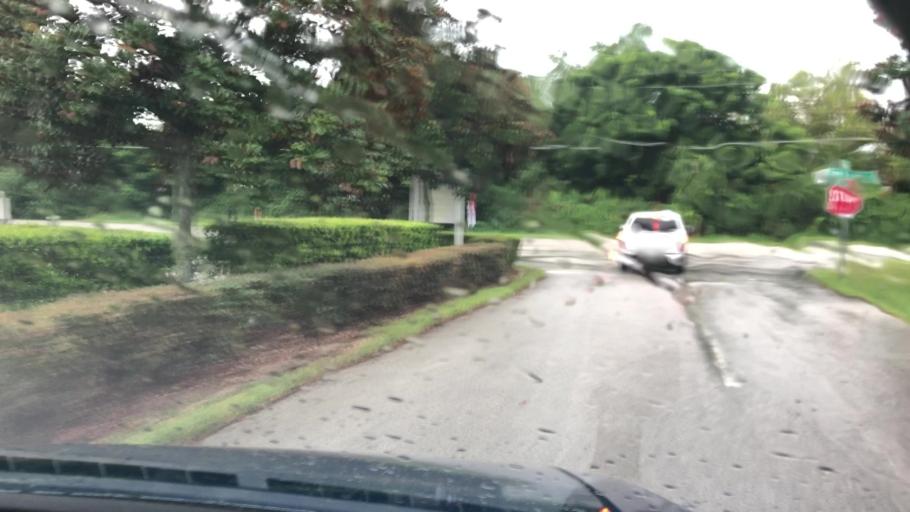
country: US
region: Florida
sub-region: Lake County
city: Eustis
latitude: 28.8792
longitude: -81.7376
